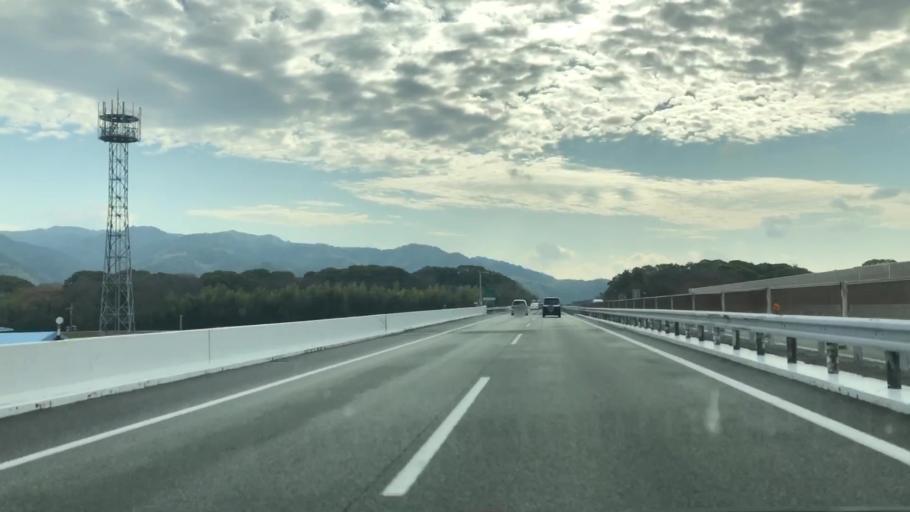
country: JP
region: Fukuoka
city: Setakamachi-takayanagi
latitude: 33.1848
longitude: 130.5188
